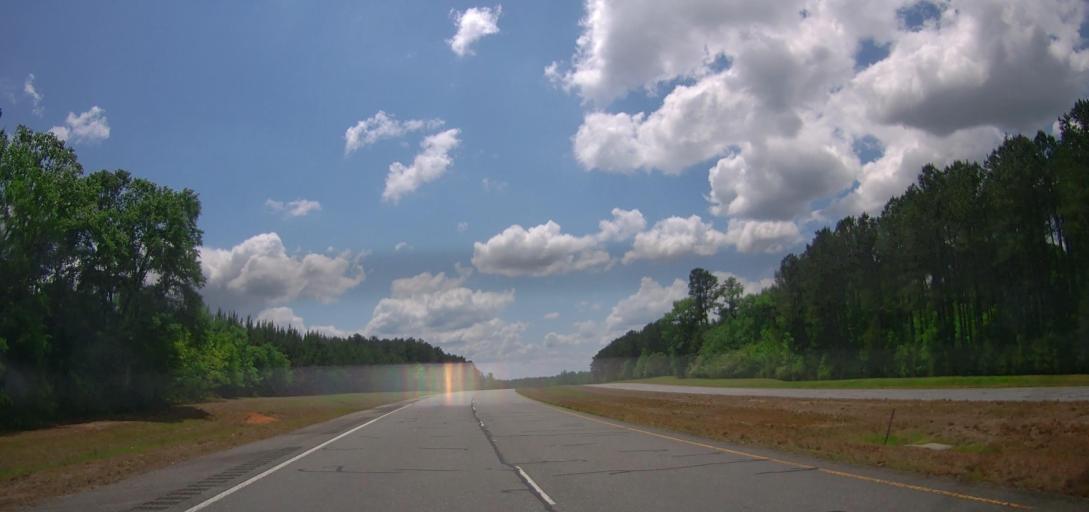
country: US
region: Georgia
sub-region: Laurens County
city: Dublin
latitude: 32.5898
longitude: -82.9573
